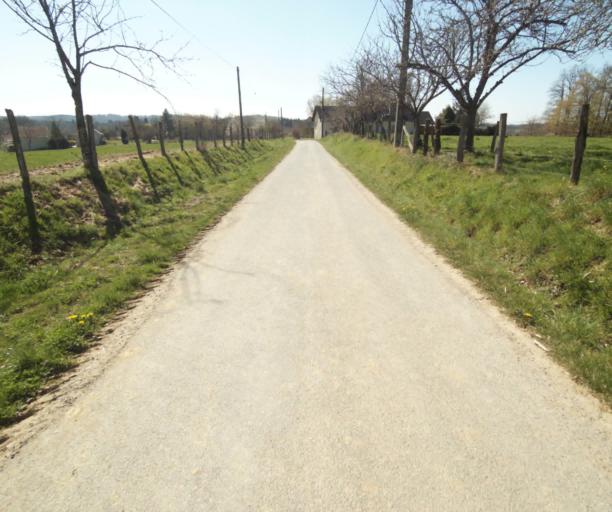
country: FR
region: Limousin
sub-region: Departement de la Correze
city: Saint-Mexant
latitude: 45.3162
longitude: 1.6568
